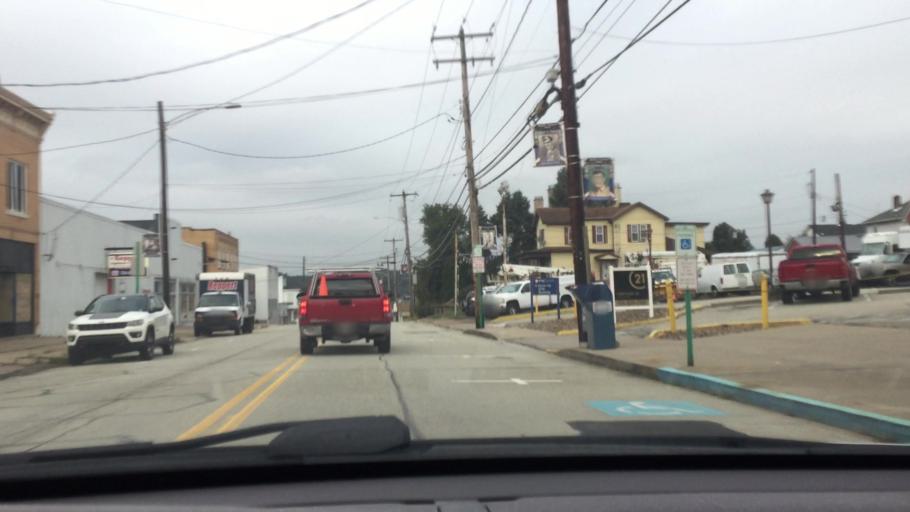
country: US
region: Pennsylvania
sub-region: Westmoreland County
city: North Belle Vernon
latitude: 40.1301
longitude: -79.8665
